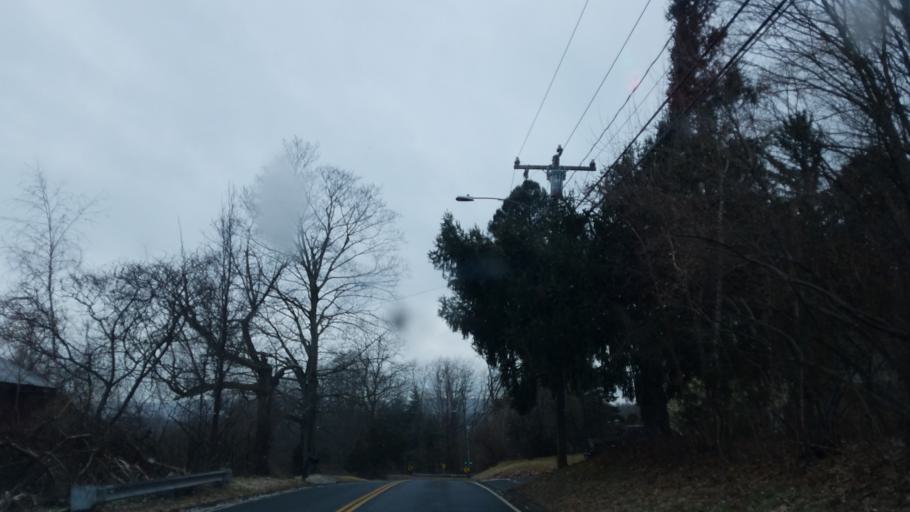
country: US
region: Connecticut
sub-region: Hartford County
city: Kensington
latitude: 41.5917
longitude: -72.7863
